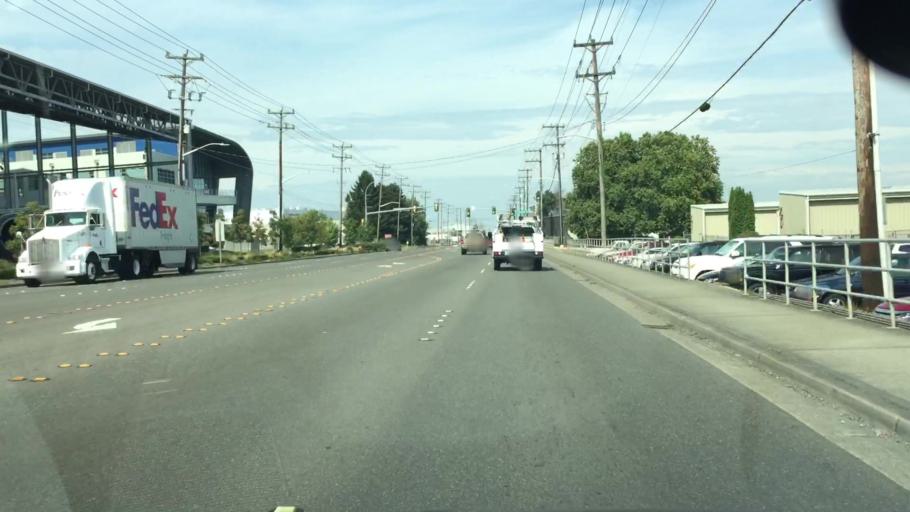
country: US
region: Washington
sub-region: King County
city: Boulevard Park
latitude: 47.5198
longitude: -122.2986
